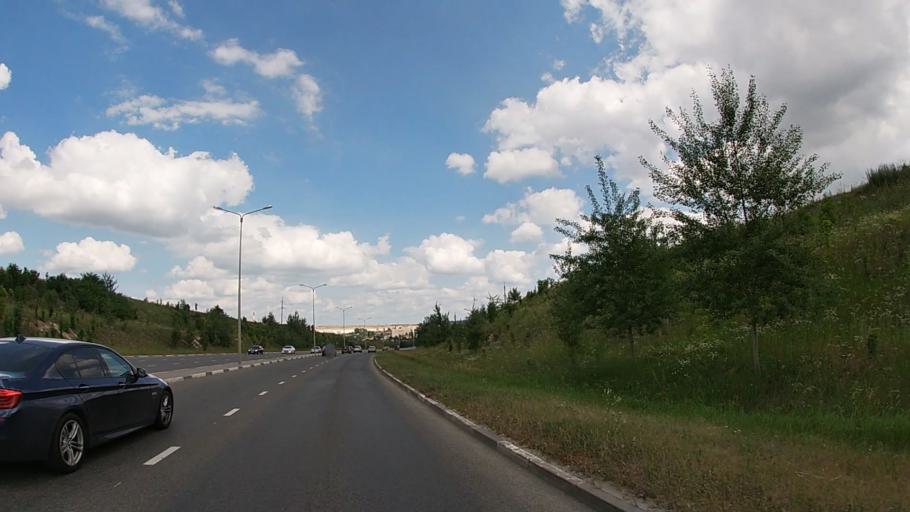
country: RU
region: Belgorod
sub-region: Belgorodskiy Rayon
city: Belgorod
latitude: 50.6030
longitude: 36.5298
